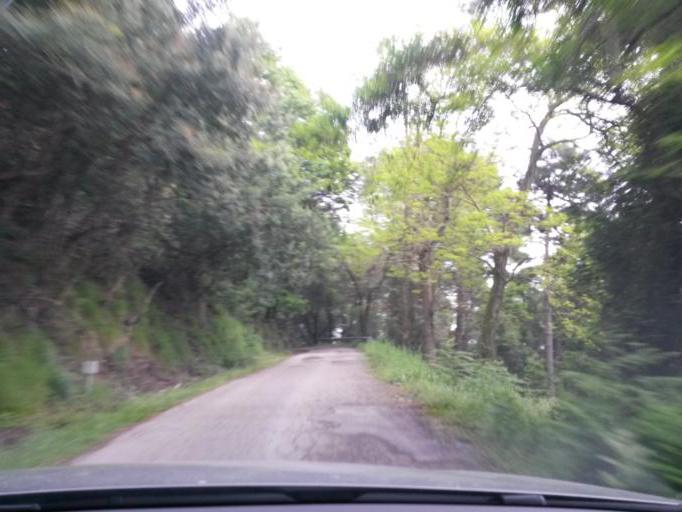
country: IT
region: Tuscany
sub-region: Provincia di Livorno
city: Marciana
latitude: 42.7715
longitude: 10.1888
